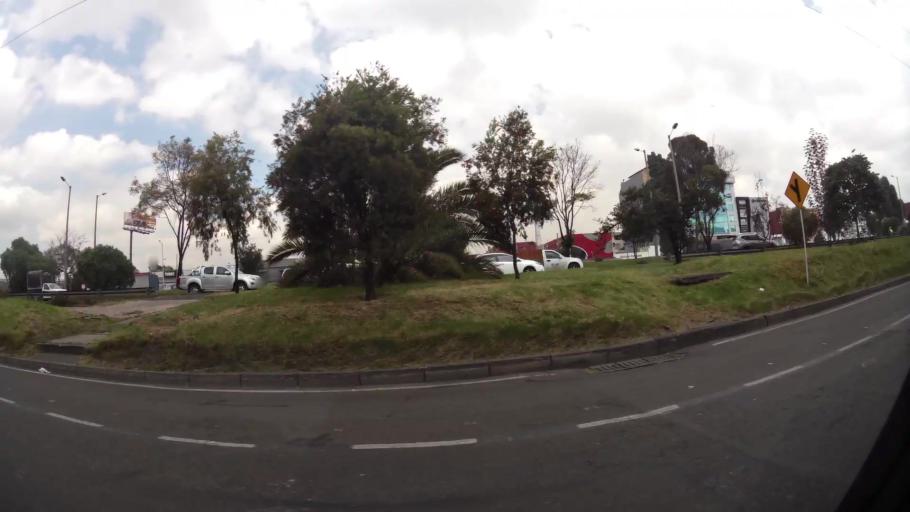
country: CO
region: Bogota D.C.
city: Barrio San Luis
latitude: 4.7027
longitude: -74.0542
